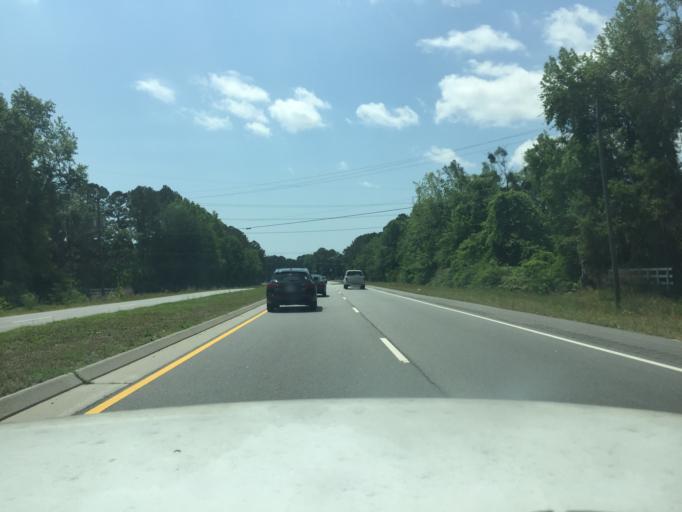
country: US
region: Georgia
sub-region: Chatham County
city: Montgomery
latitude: 31.9617
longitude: -81.0995
